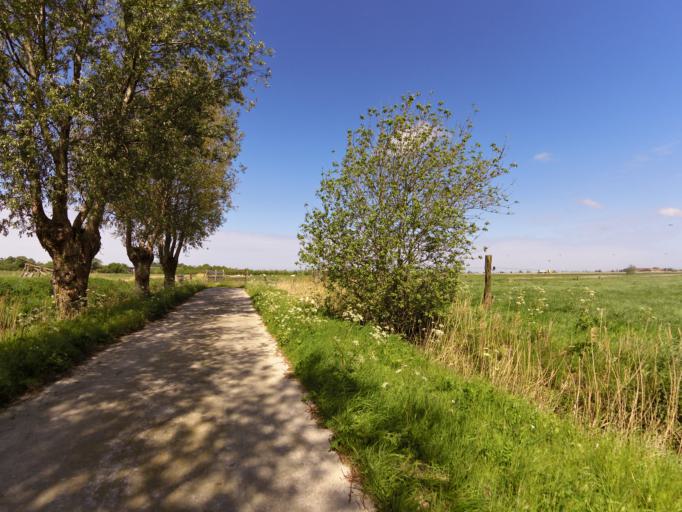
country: BE
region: Flanders
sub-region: Provincie West-Vlaanderen
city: Middelkerke
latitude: 51.1361
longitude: 2.8496
